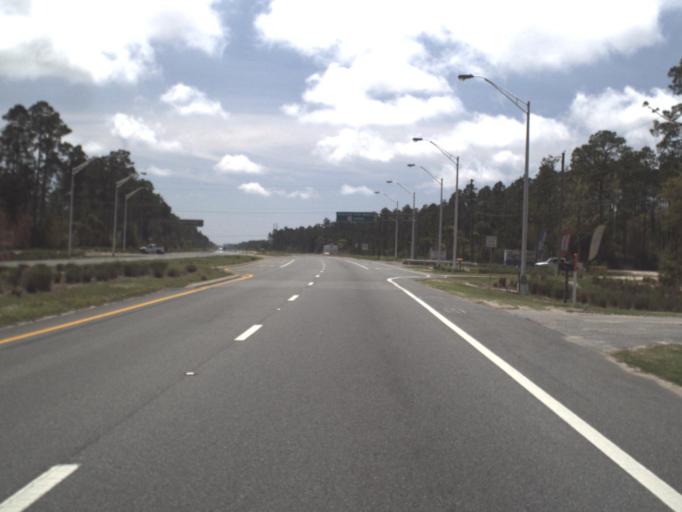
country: US
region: Florida
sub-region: Bay County
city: Laguna Beach
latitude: 30.2908
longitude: -85.8614
